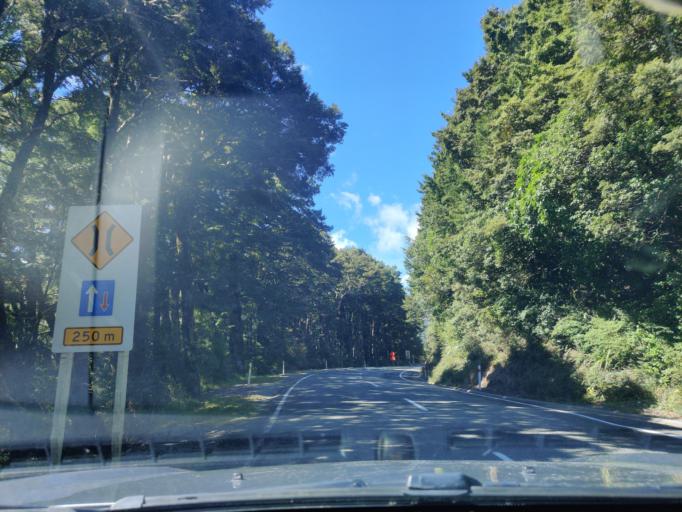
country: NZ
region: Canterbury
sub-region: Hurunui District
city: Amberley
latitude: -42.3738
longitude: 172.3741
